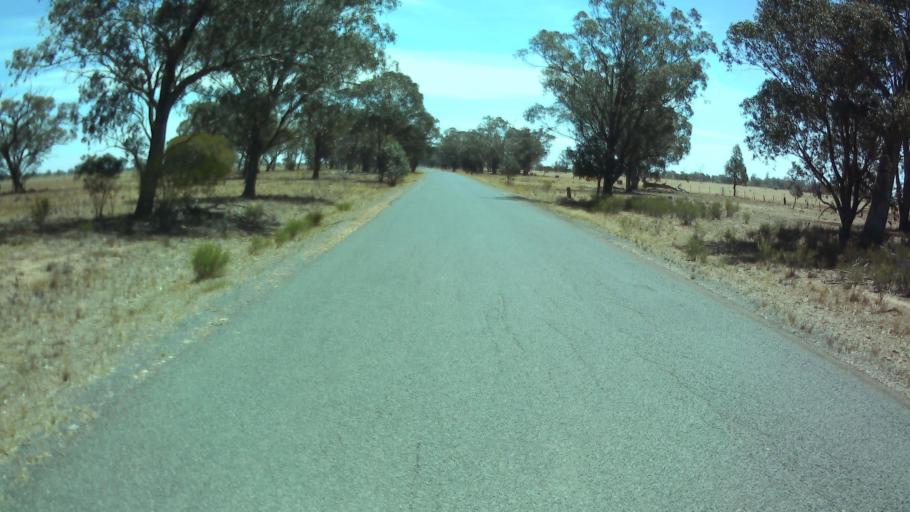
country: AU
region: New South Wales
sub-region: Weddin
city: Grenfell
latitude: -34.0012
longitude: 147.7496
